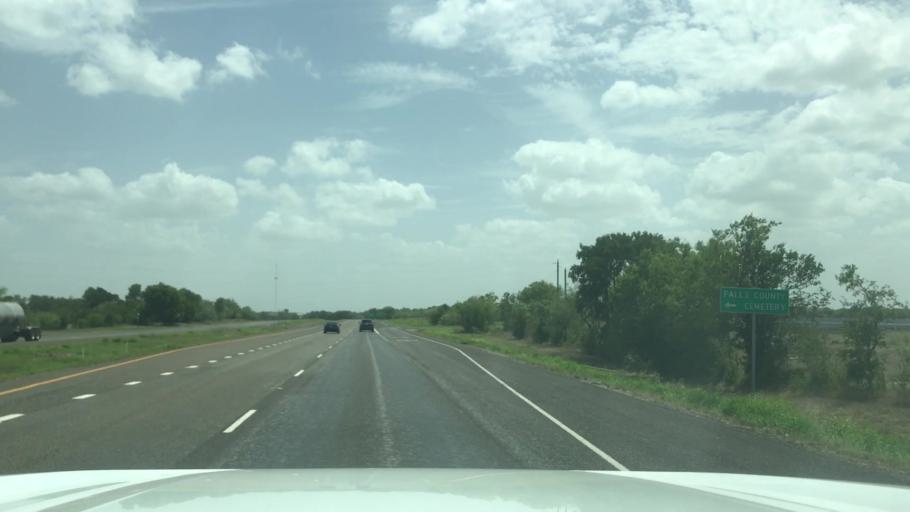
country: US
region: Texas
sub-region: Falls County
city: Marlin
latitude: 31.2864
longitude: -96.8753
